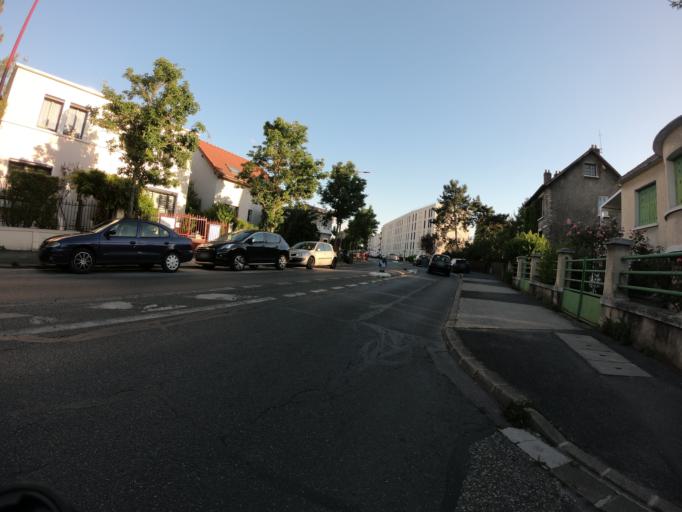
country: FR
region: Ile-de-France
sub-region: Departement du Val-de-Marne
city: Fresnes
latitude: 48.7553
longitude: 2.3133
